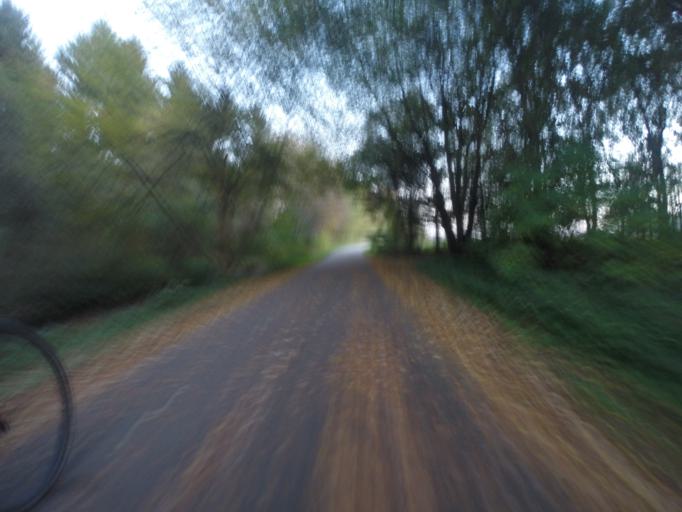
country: DK
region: Capital Region
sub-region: Albertslund Kommune
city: Albertslund
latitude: 55.6492
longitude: 12.3356
